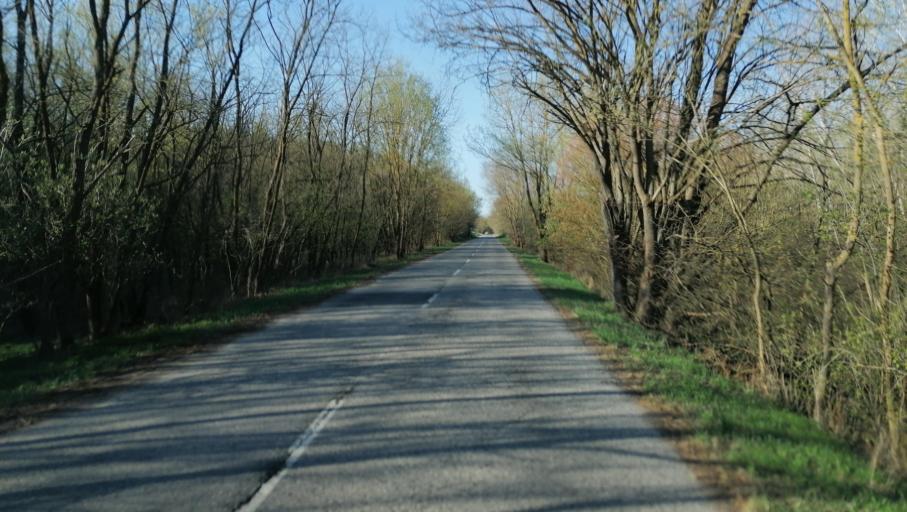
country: HU
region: Pest
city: Szentendre
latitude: 47.6779
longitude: 19.0928
